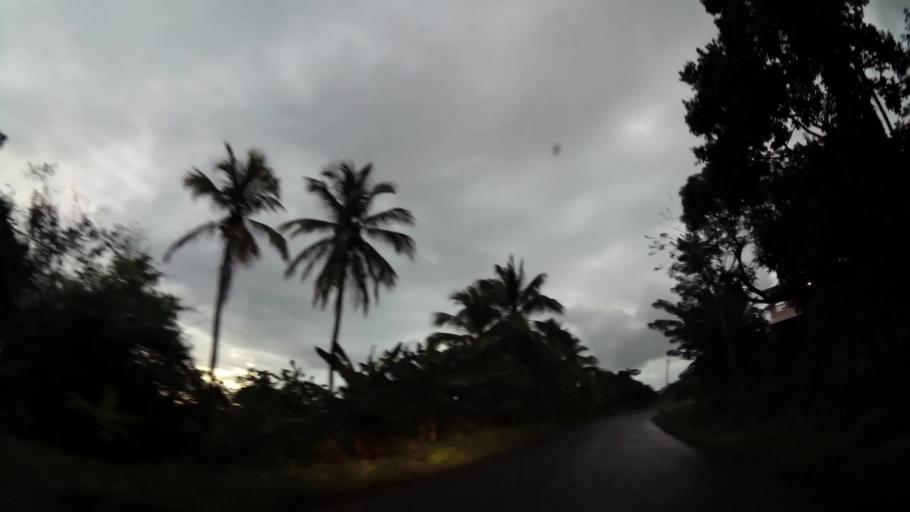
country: DM
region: Saint Andrew
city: Wesley
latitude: 15.5854
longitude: -61.3237
